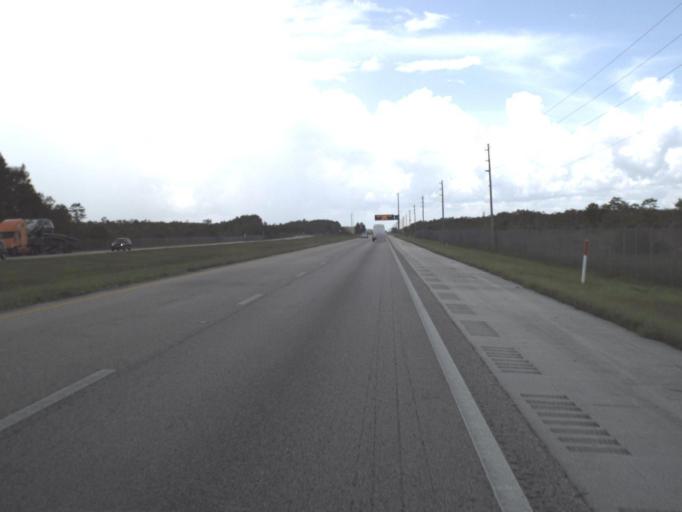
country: US
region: Florida
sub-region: Collier County
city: Immokalee
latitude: 26.1694
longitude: -81.0388
